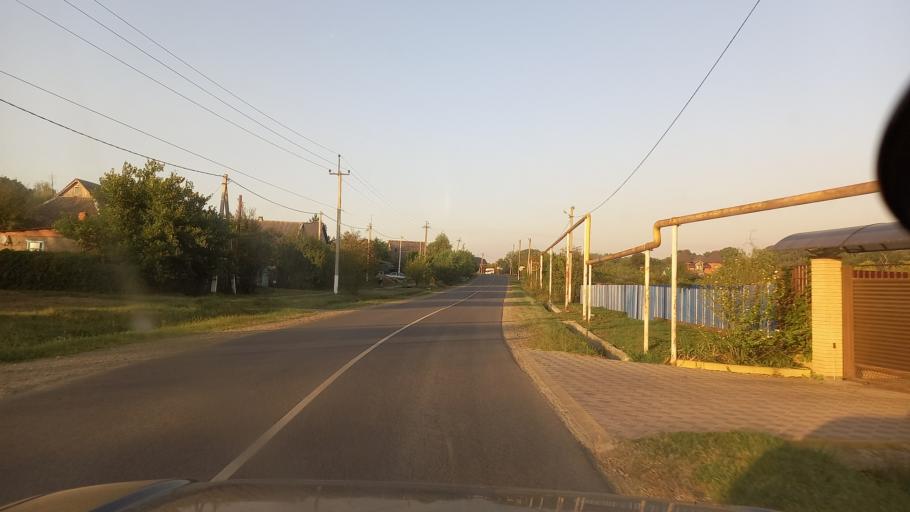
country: RU
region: Krasnodarskiy
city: Smolenskaya
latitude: 44.7683
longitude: 38.7801
